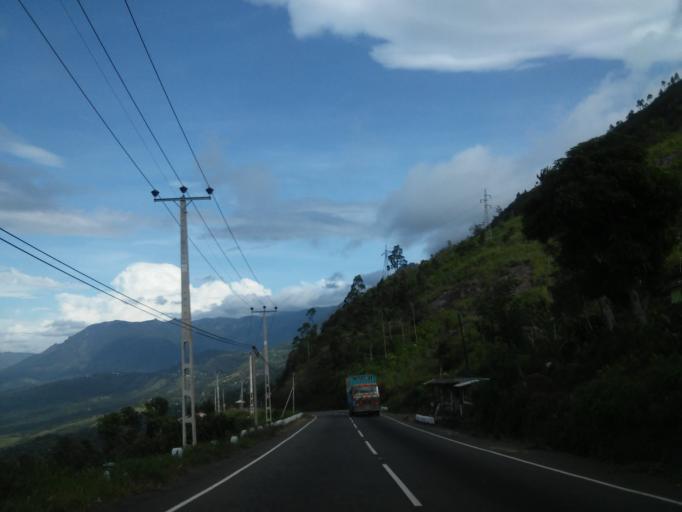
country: LK
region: Uva
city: Haputale
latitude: 6.7594
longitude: 80.9401
